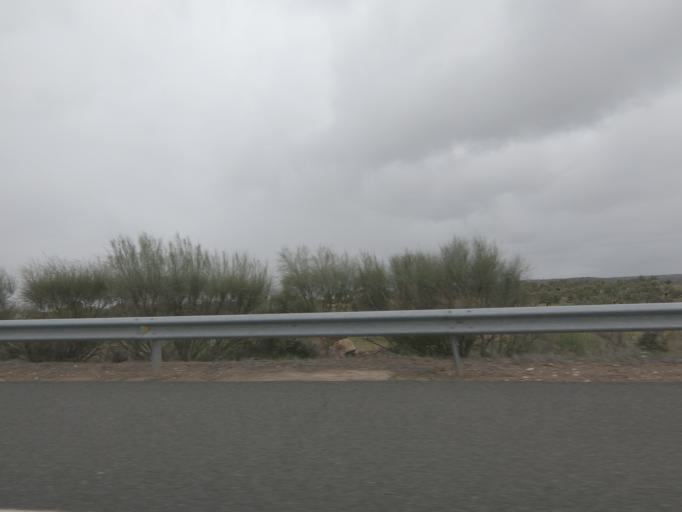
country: ES
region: Extremadura
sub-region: Provincia de Caceres
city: Plasencia
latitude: 40.0560
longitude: -6.1289
